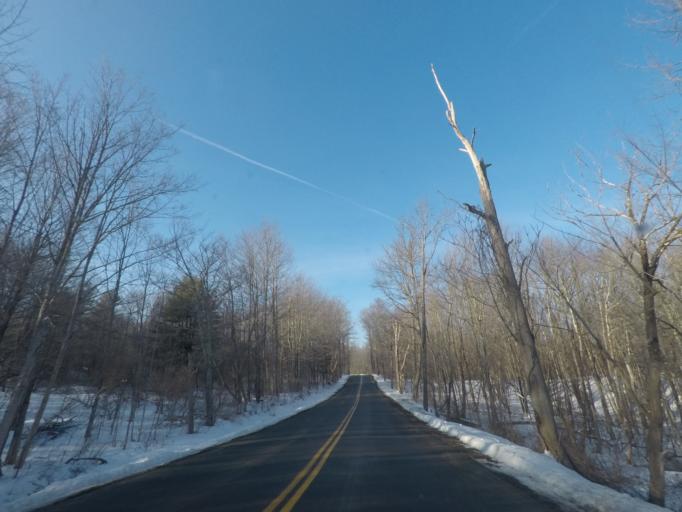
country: US
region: Massachusetts
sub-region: Berkshire County
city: Richmond
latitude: 42.5243
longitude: -73.3803
